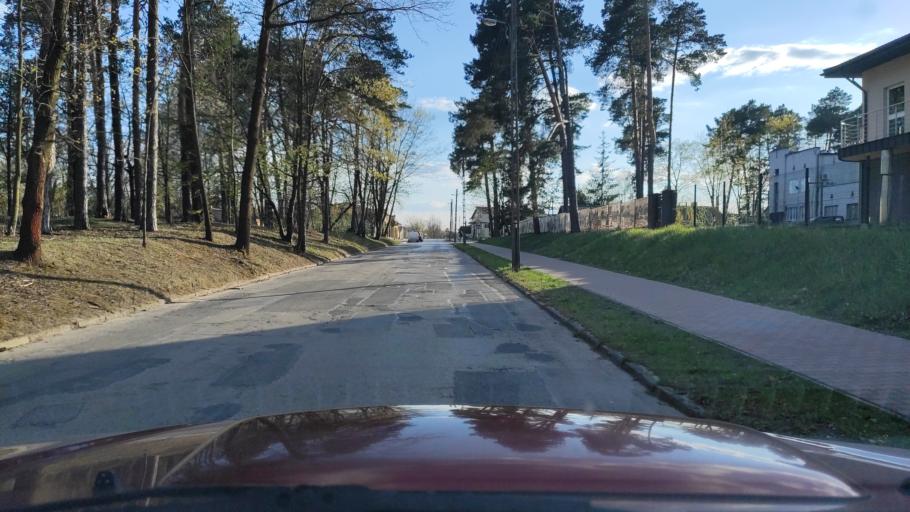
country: PL
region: Masovian Voivodeship
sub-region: Powiat radomski
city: Pionki
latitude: 51.4754
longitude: 21.4460
